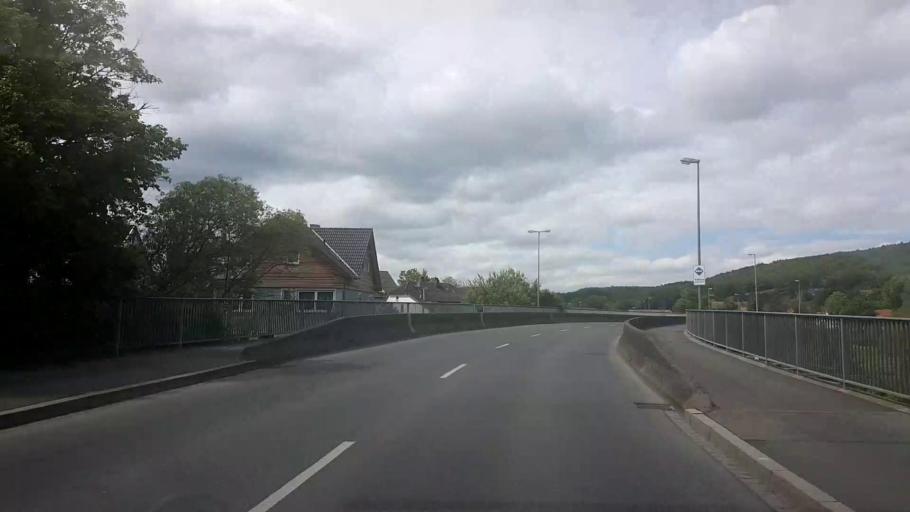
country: DE
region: Bavaria
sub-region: Upper Franconia
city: Lichtenfels
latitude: 50.1518
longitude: 11.0623
